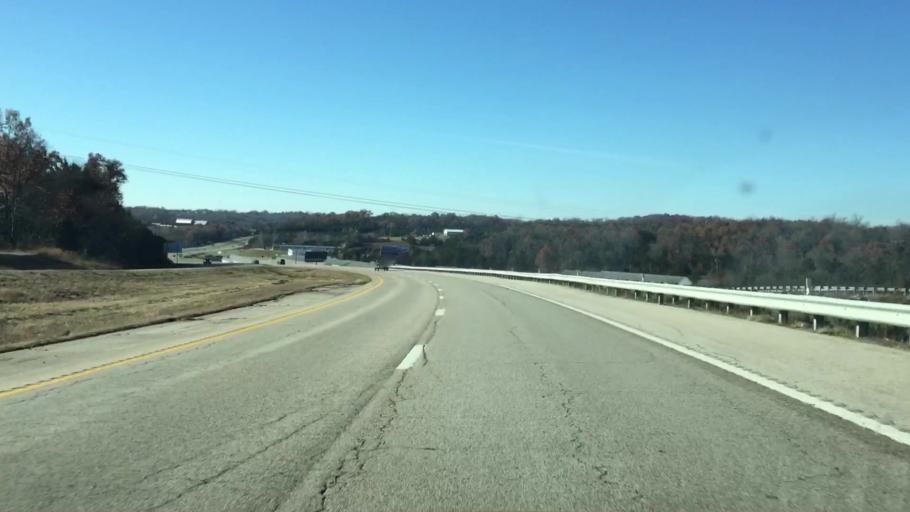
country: US
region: Missouri
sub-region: Cole County
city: Jefferson City
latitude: 38.5345
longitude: -92.2172
